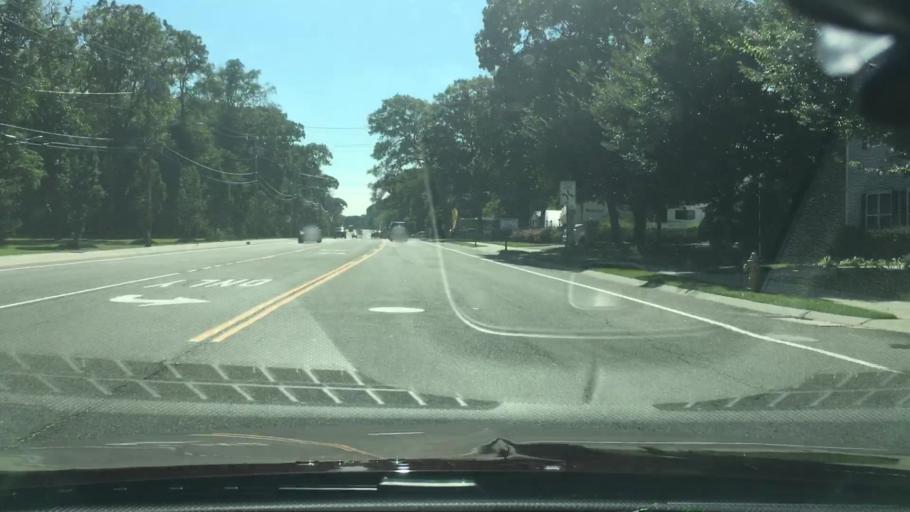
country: US
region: New York
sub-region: Suffolk County
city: Coram
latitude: 40.8820
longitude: -73.0110
